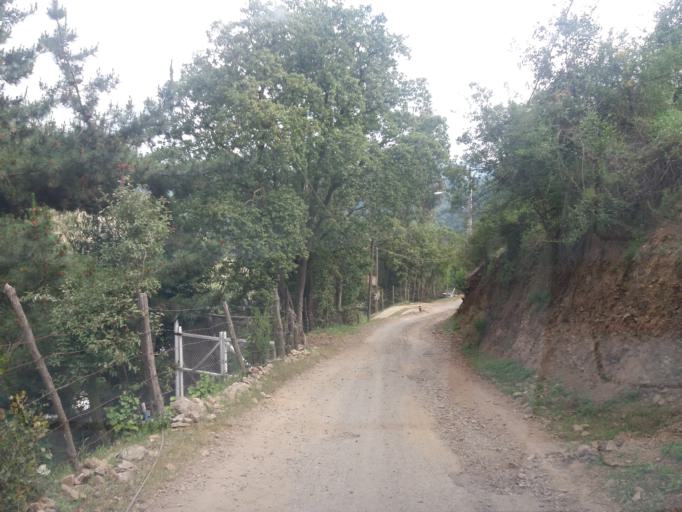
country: CL
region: Valparaiso
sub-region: Provincia de Marga Marga
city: Limache
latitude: -33.0752
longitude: -71.0618
